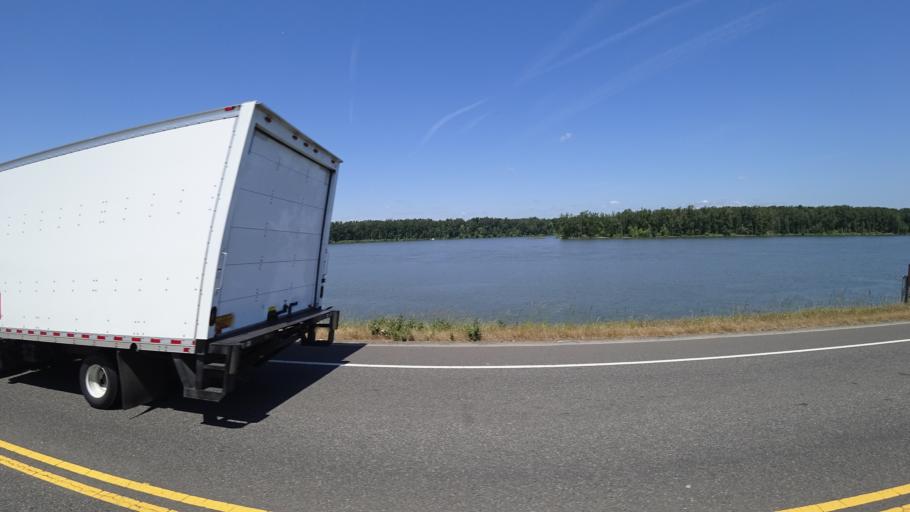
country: US
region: Oregon
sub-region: Multnomah County
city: Fairview
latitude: 45.5597
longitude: -122.4858
